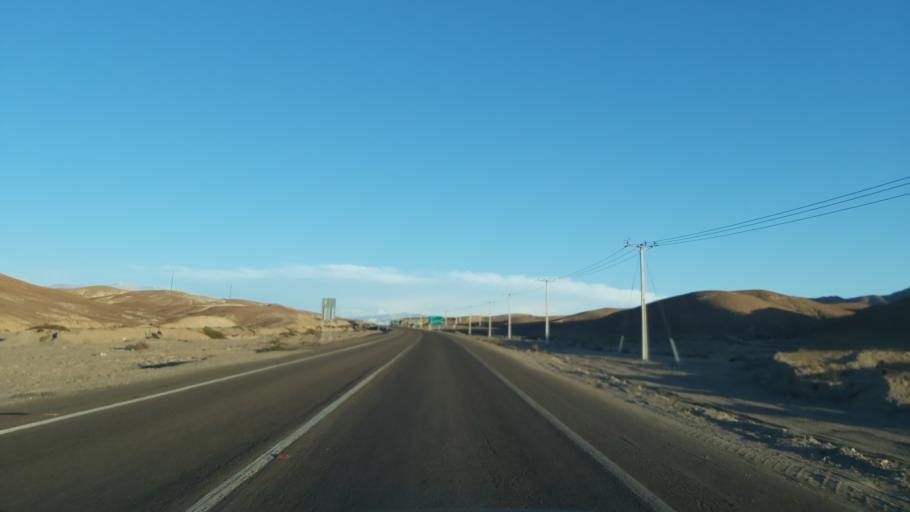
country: CL
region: Atacama
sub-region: Provincia de Chanaral
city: Diego de Almagro
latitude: -26.4147
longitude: -70.0324
